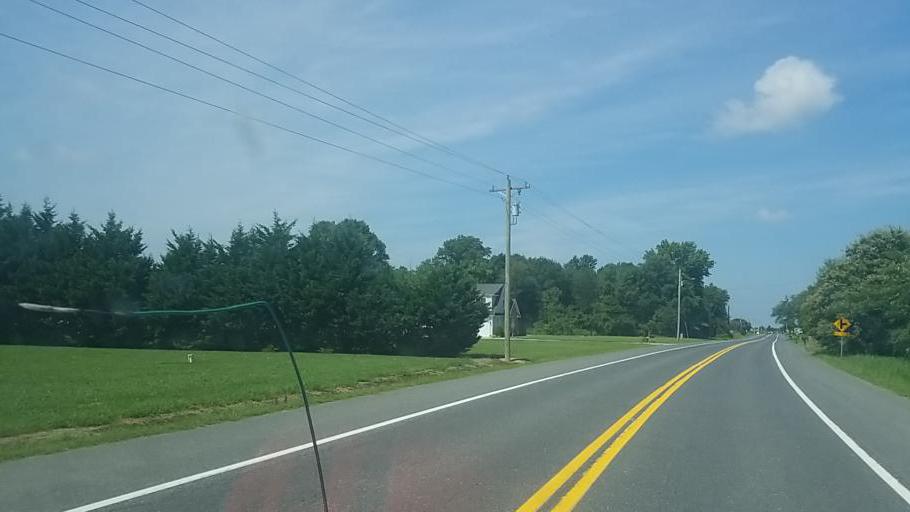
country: US
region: Delaware
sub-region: Sussex County
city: Bridgeville
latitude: 38.8240
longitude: -75.6426
